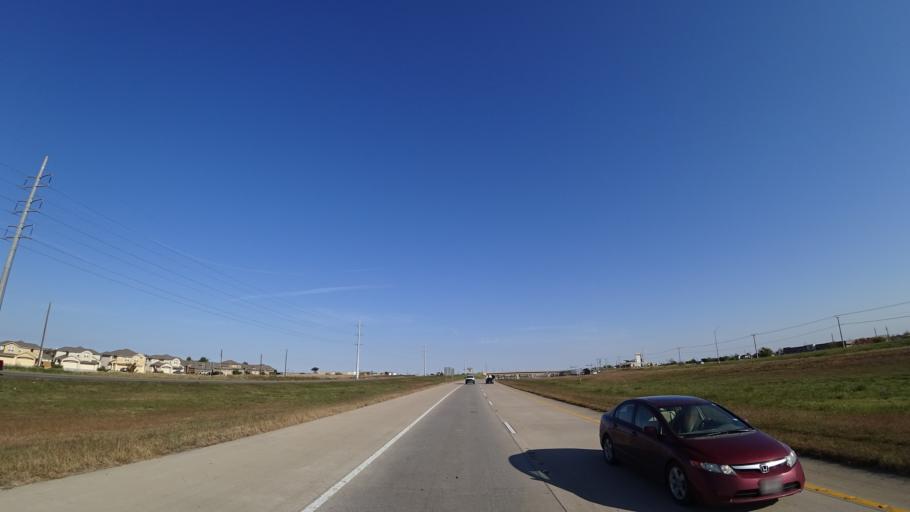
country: US
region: Texas
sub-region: Williamson County
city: Hutto
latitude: 30.4968
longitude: -97.5829
